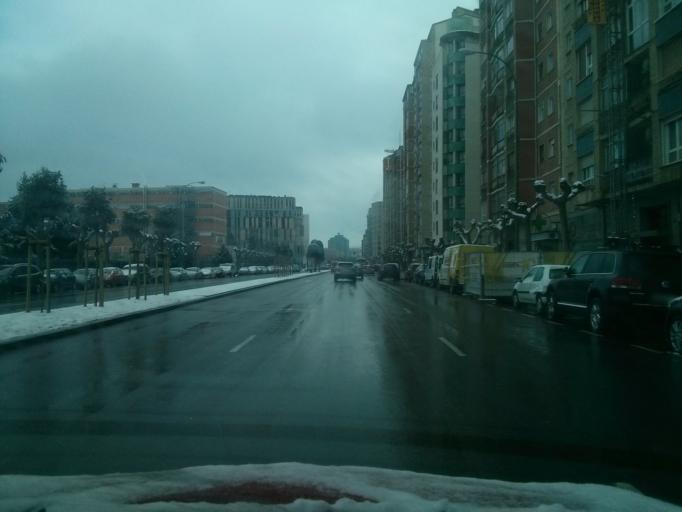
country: ES
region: Castille and Leon
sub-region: Provincia de Burgos
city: Burgos
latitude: 42.3524
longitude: -3.6905
